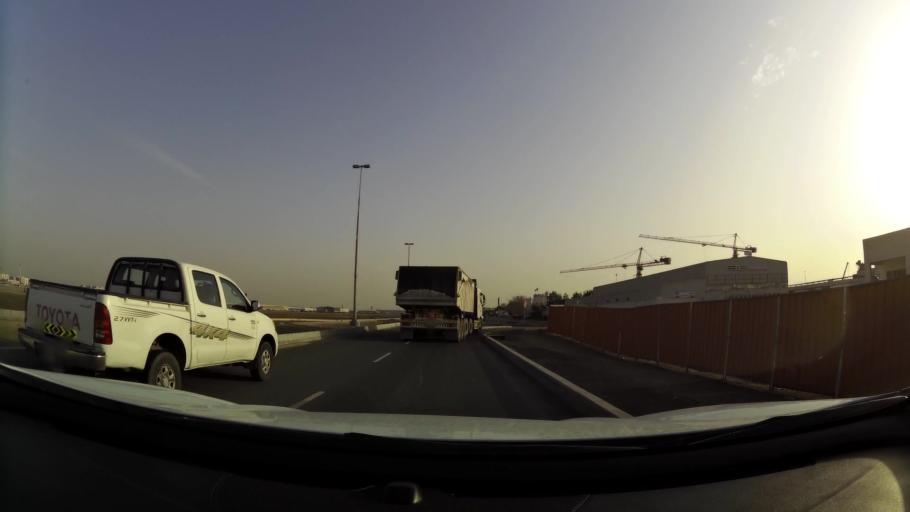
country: AE
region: Abu Dhabi
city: Abu Dhabi
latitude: 24.3444
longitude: 54.5123
